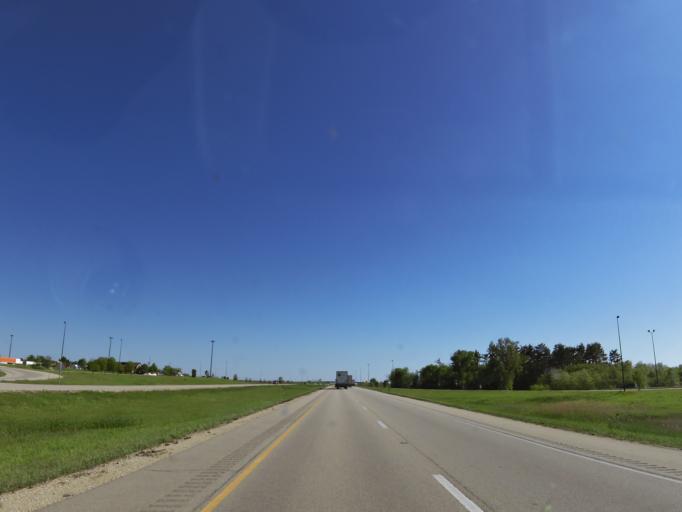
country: US
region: Illinois
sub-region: LaSalle County
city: Earlville
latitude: 41.7270
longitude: -89.0091
